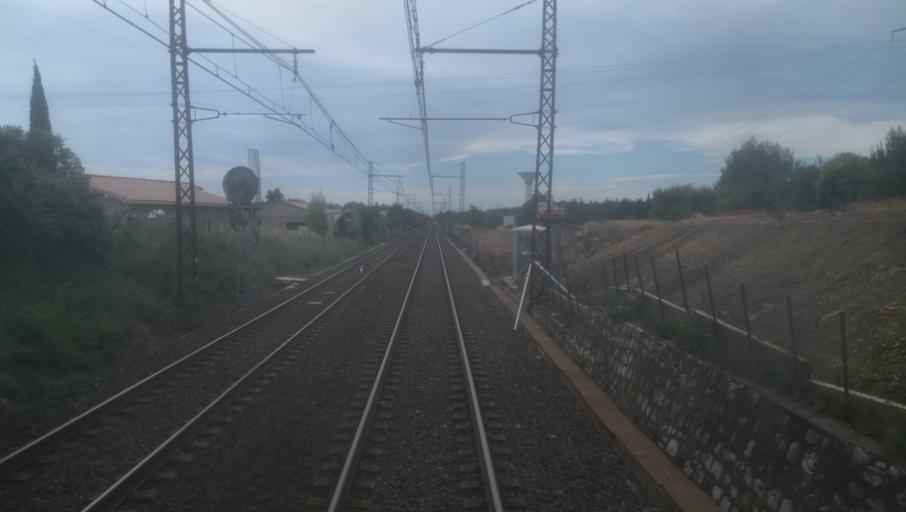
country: FR
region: Languedoc-Roussillon
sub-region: Departement de l'Herault
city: Lunel-Viel
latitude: 43.6798
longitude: 4.0853
